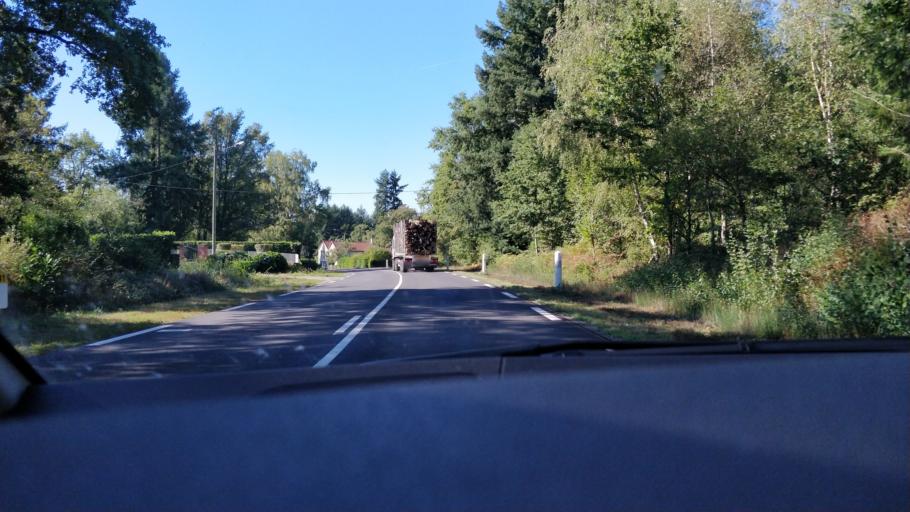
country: FR
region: Limousin
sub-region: Departement de la Haute-Vienne
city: Sauviat-sur-Vige
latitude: 45.8999
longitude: 1.5857
